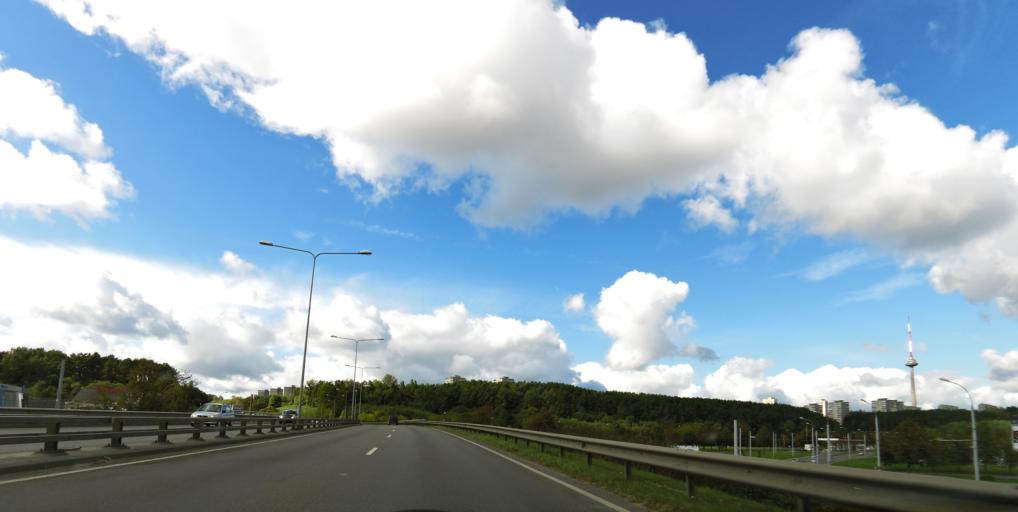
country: LT
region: Vilnius County
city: Lazdynai
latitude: 54.6715
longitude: 25.2252
